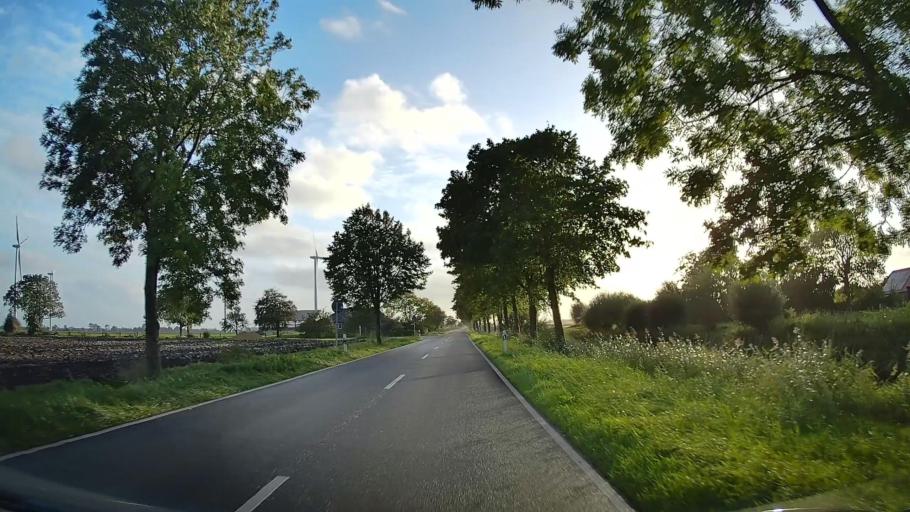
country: DE
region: Schleswig-Holstein
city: Sommerland
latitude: 53.8015
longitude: 9.5265
